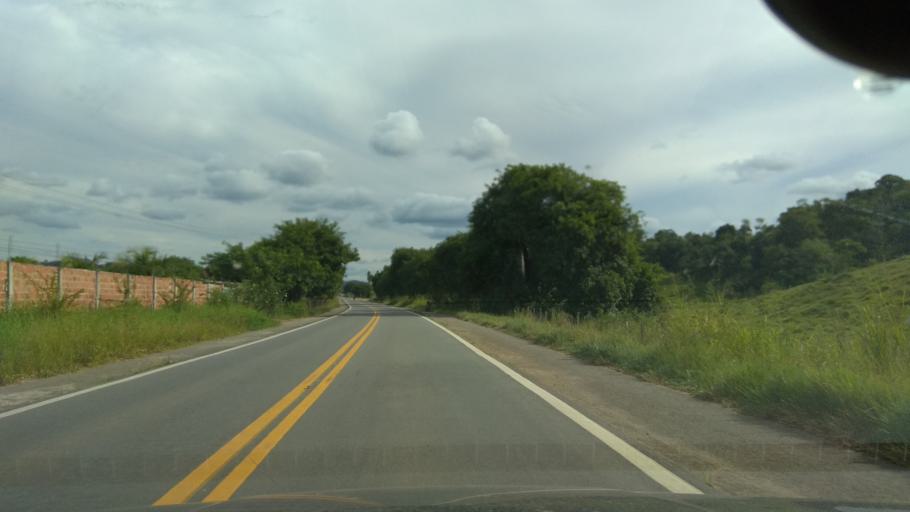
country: BR
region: Bahia
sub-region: Jitauna
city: Jitauna
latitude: -14.0109
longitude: -39.8786
